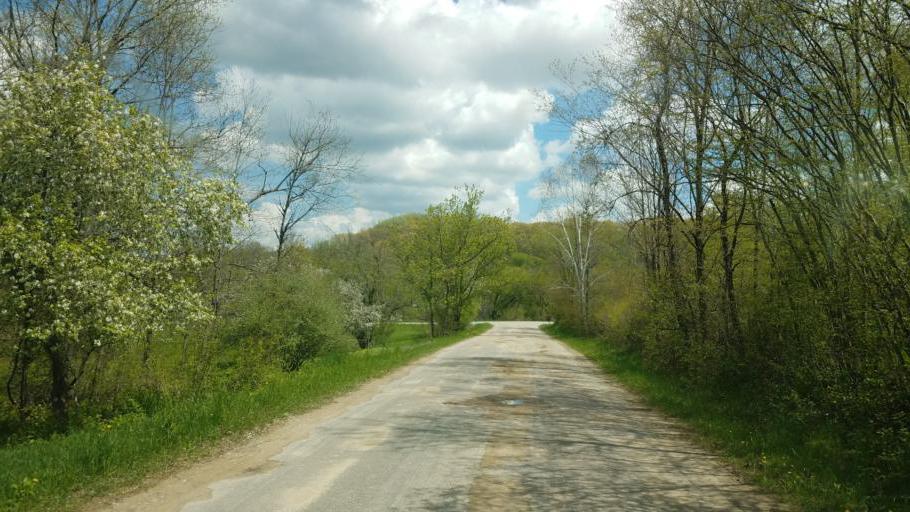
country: US
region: Wisconsin
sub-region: Vernon County
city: Hillsboro
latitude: 43.5976
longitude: -90.3699
